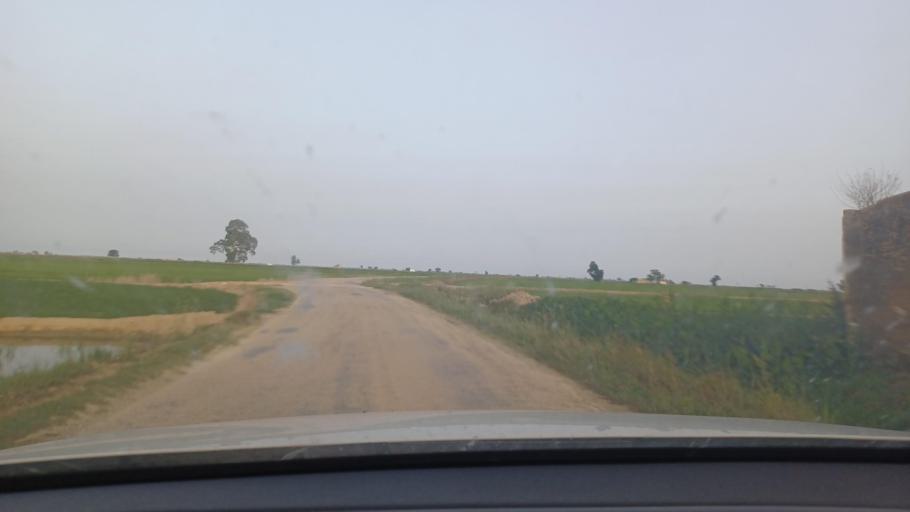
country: ES
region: Catalonia
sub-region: Provincia de Tarragona
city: Deltebre
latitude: 40.6961
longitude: 0.6488
